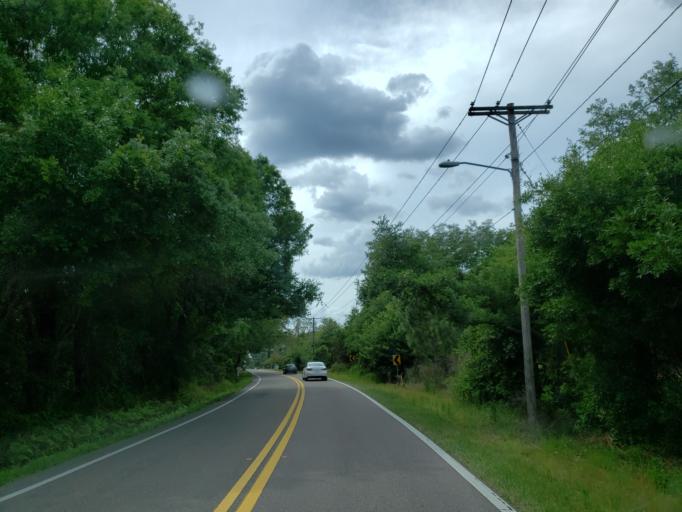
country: US
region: Florida
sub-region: Hillsborough County
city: Keystone
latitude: 28.1312
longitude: -82.6186
